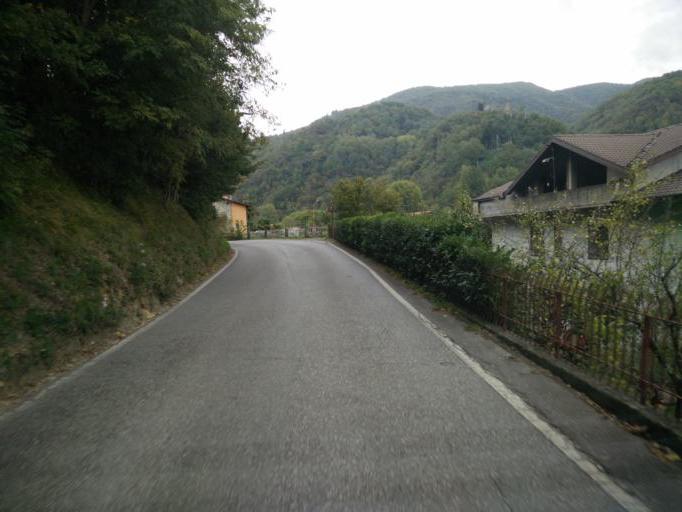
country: IT
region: Tuscany
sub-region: Provincia di Massa-Carrara
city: Casola in Lunigiana
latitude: 44.1925
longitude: 10.1486
